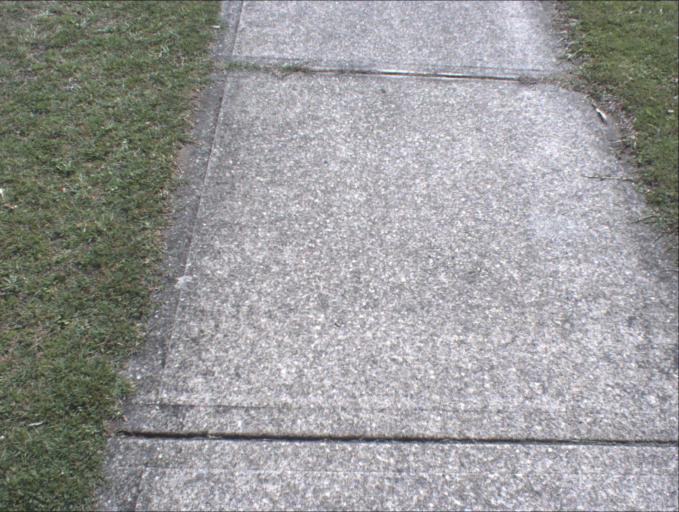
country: AU
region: Queensland
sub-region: Logan
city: Waterford West
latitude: -27.6956
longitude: 153.1577
